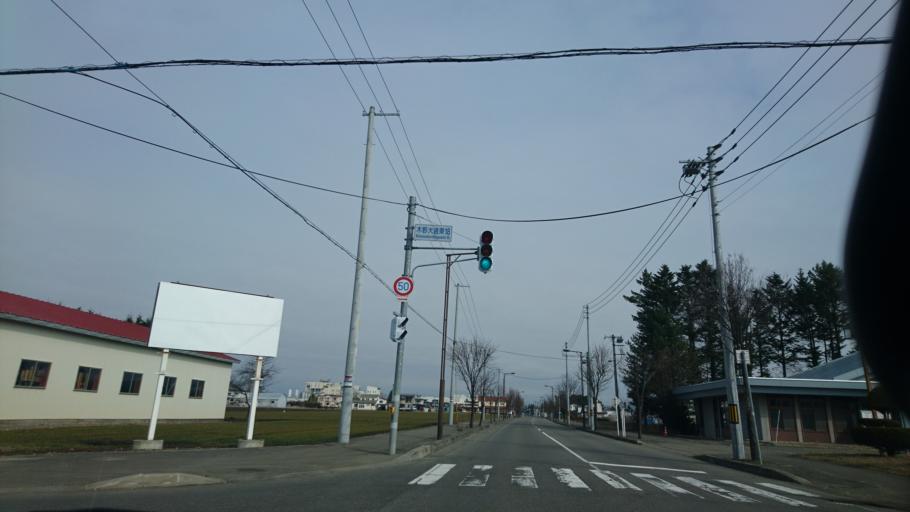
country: JP
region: Hokkaido
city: Otofuke
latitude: 42.9728
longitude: 143.2123
